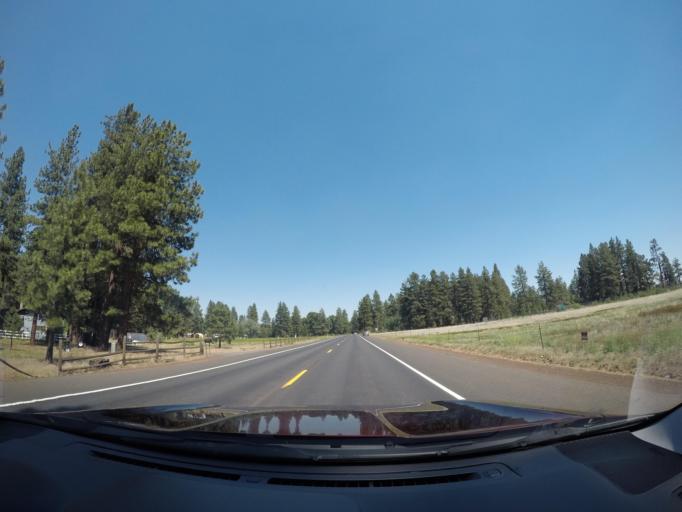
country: US
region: Oregon
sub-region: Deschutes County
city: Sisters
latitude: 44.2878
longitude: -121.5272
